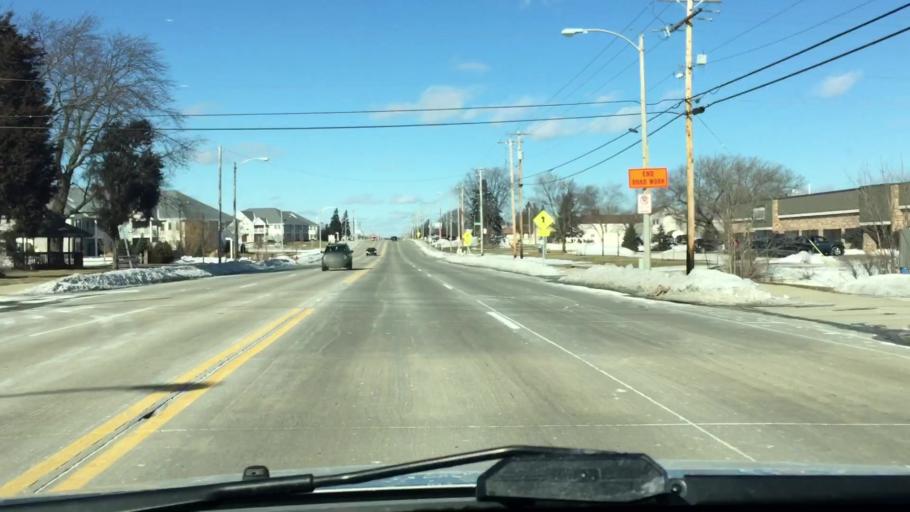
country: US
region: Wisconsin
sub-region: Milwaukee County
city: Greendale
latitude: 42.9179
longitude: -87.9307
